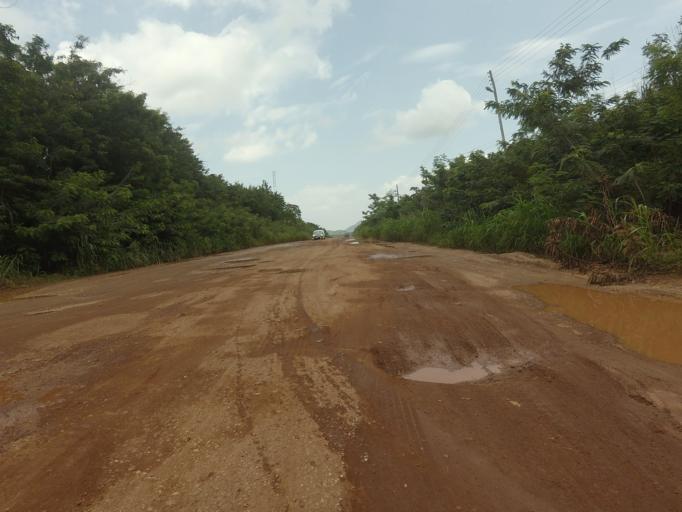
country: GH
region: Volta
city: Ho
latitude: 6.6810
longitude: 0.3286
